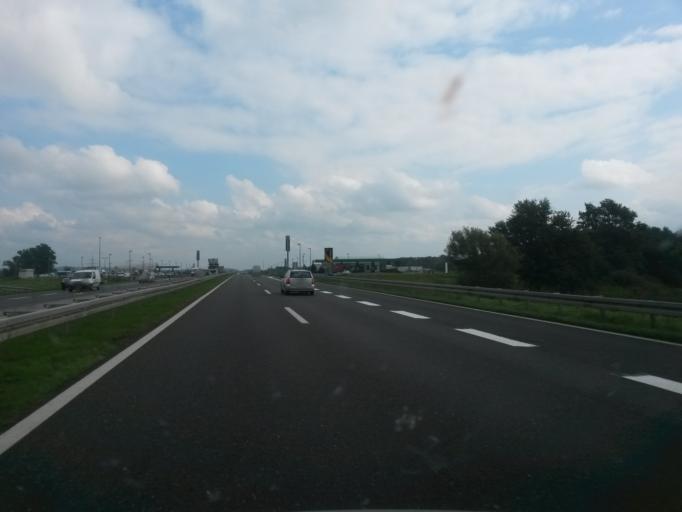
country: HR
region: Grad Zagreb
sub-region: Sesvete
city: Sesvete
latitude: 45.8682
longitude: 16.1890
